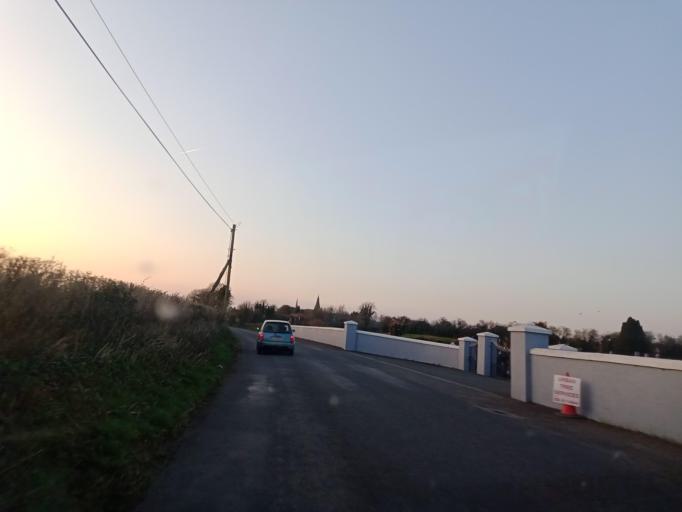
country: IE
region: Leinster
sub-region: Laois
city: Abbeyleix
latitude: 52.8702
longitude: -7.3045
